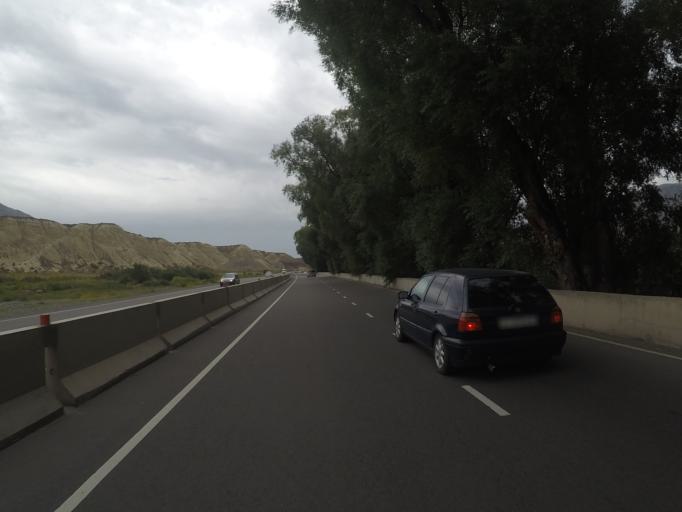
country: KG
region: Ysyk-Koel
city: Balykchy
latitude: 42.4675
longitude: 75.9082
